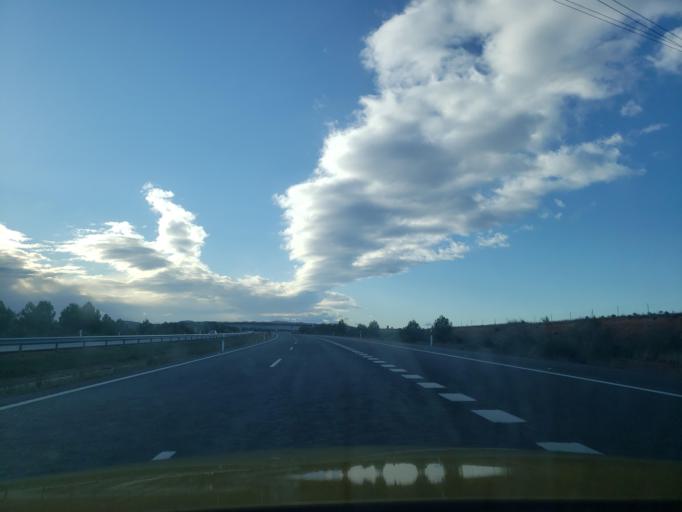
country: ES
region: Castille-La Mancha
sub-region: Province of Toledo
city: Consuegra
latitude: 39.4767
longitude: -3.5878
